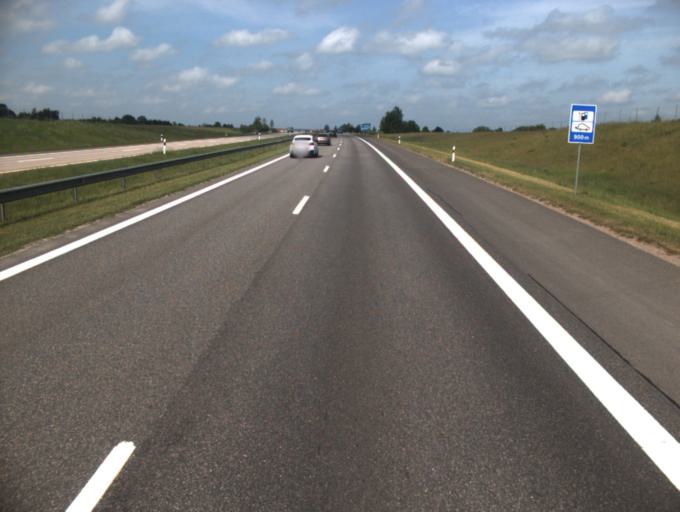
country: LT
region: Klaipedos apskritis
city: Gargzdai
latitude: 55.7316
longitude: 21.3985
